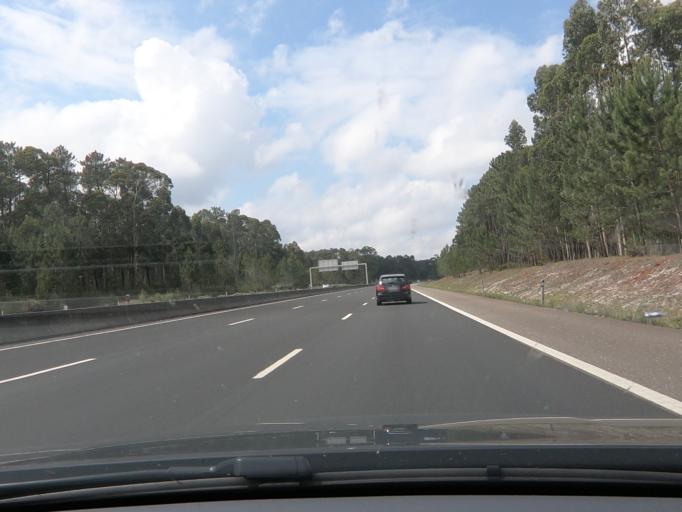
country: PT
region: Leiria
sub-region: Leiria
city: Maceira
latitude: 39.7023
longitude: -8.9218
